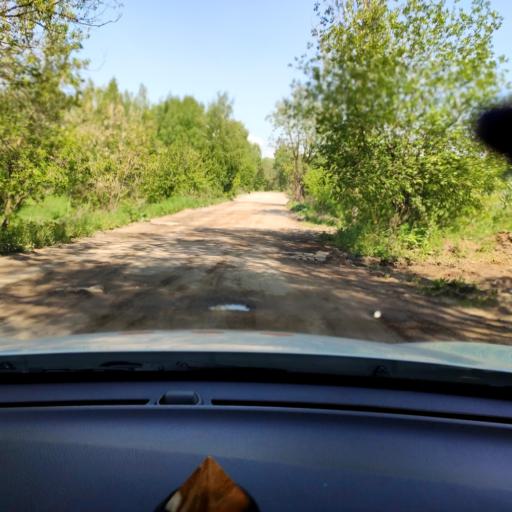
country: RU
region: Tatarstan
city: Stolbishchi
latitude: 55.7088
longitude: 49.1888
